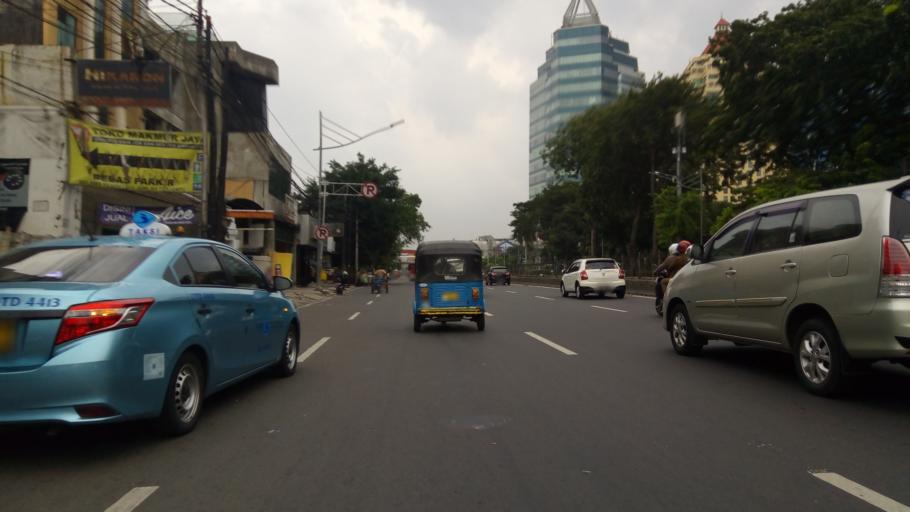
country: ID
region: Jakarta Raya
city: Jakarta
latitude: -6.1709
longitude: 106.8404
